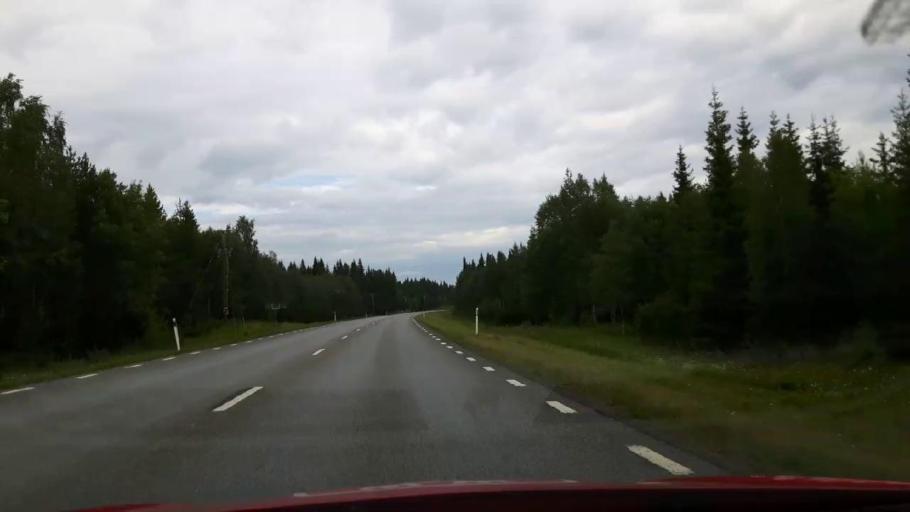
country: SE
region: Jaemtland
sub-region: Stroemsunds Kommun
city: Stroemsund
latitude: 63.6148
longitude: 15.3567
